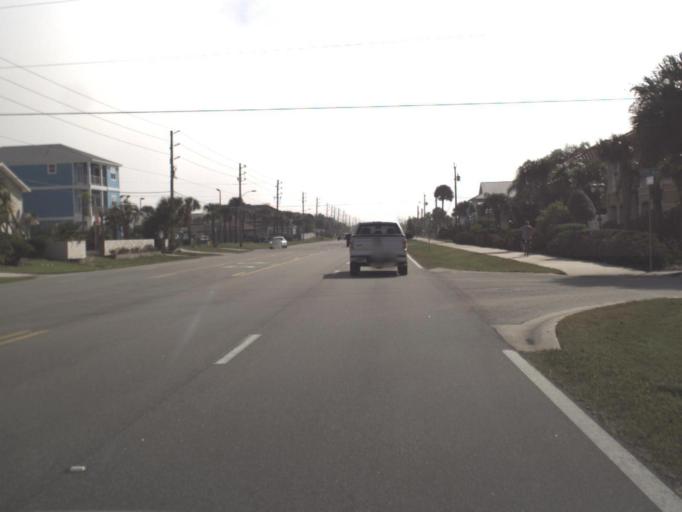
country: US
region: Florida
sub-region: Volusia County
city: Edgewater
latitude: 29.0160
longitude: -80.8837
